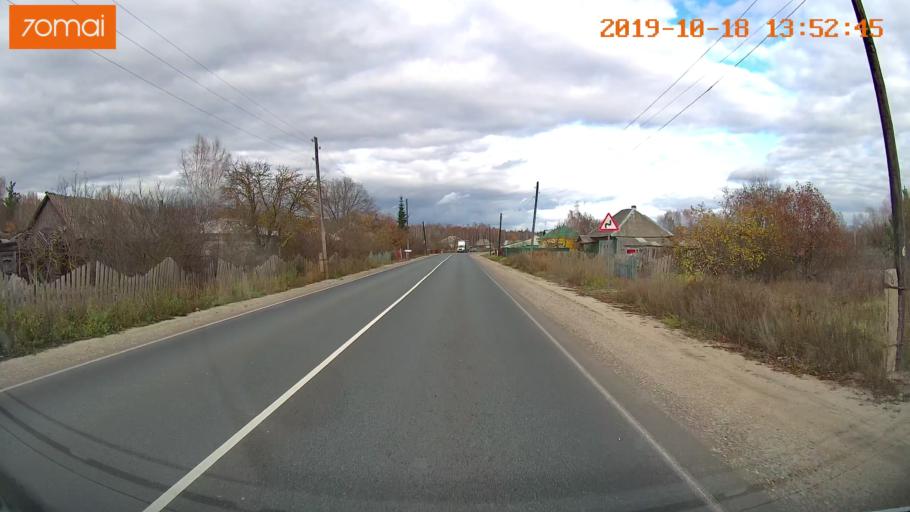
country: RU
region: Moskovskaya
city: Radovitskiy
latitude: 55.0323
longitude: 39.9706
